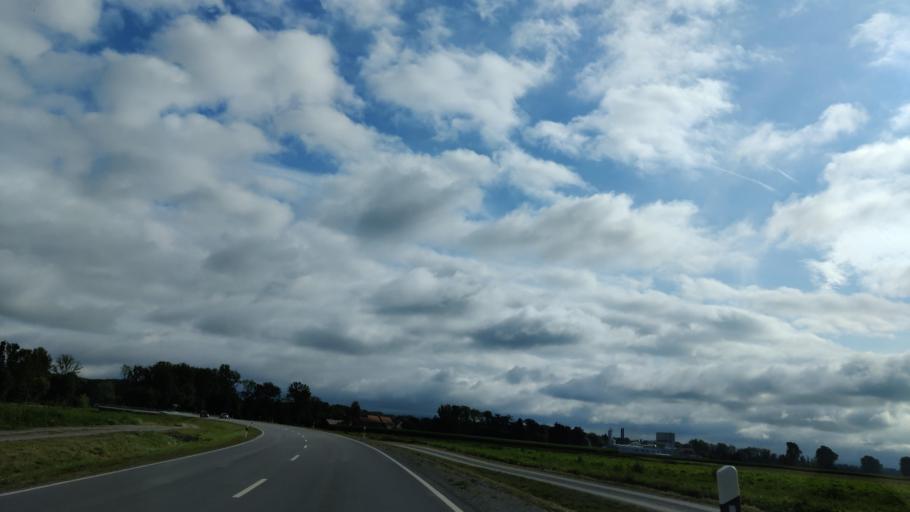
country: DE
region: Bavaria
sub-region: Lower Bavaria
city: Plattling
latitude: 48.7686
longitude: 12.8936
